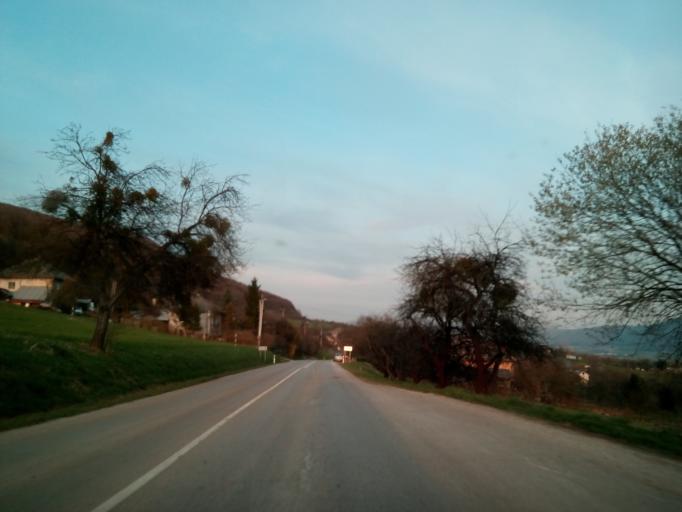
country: SK
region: Kosicky
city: Roznava
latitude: 48.6621
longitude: 20.4556
